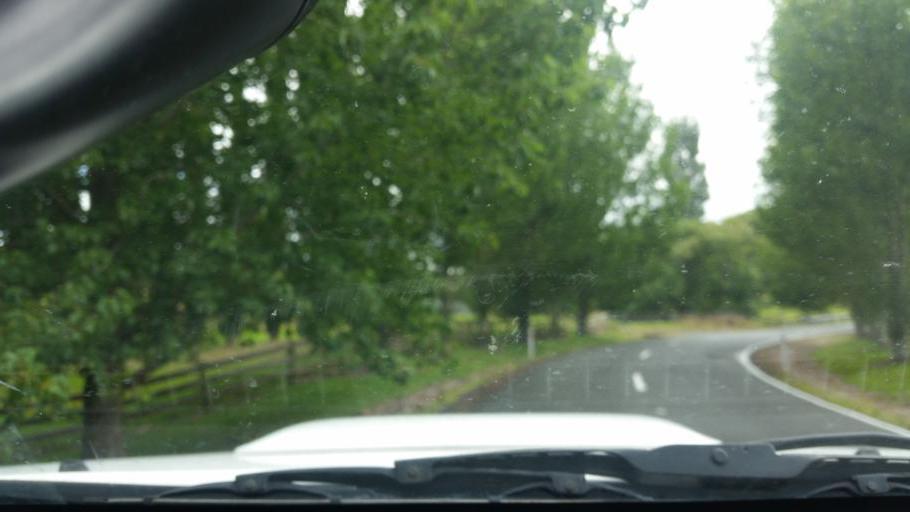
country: NZ
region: Auckland
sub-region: Auckland
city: Wellsford
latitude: -36.1313
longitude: 174.3604
